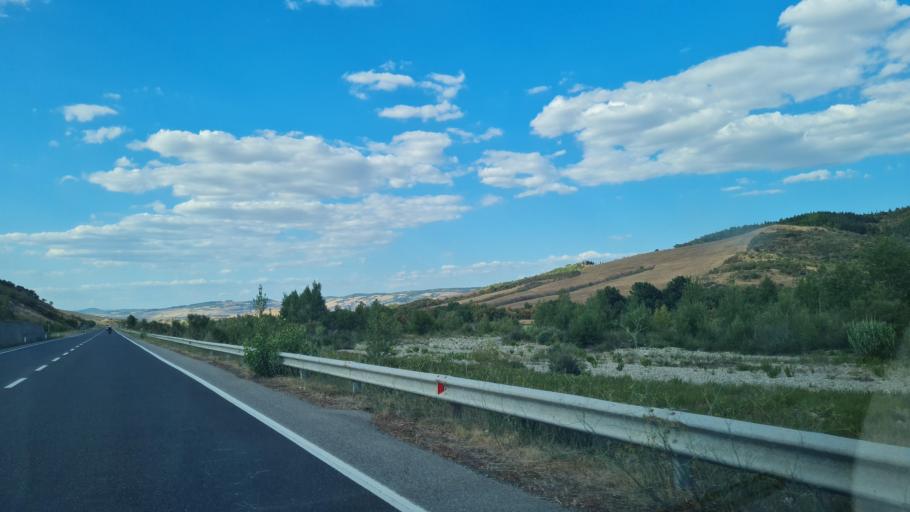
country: IT
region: Tuscany
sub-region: Provincia di Siena
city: Abbadia San Salvatore
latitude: 42.9628
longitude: 11.7060
